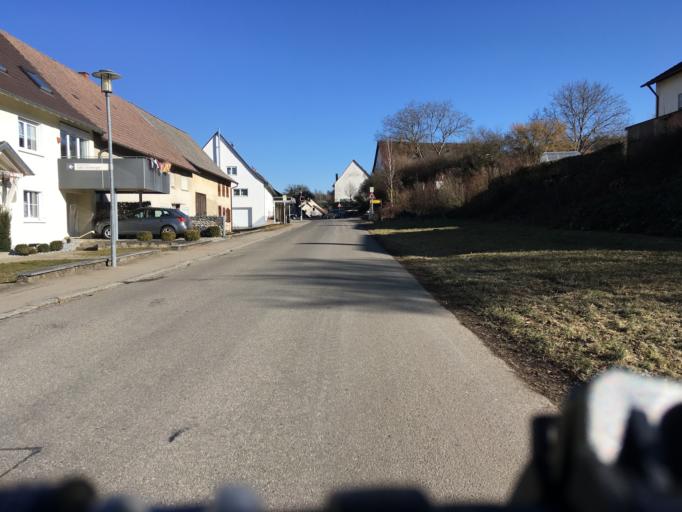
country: DE
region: Baden-Wuerttemberg
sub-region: Freiburg Region
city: Gottmadingen
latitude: 47.7510
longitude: 8.7550
